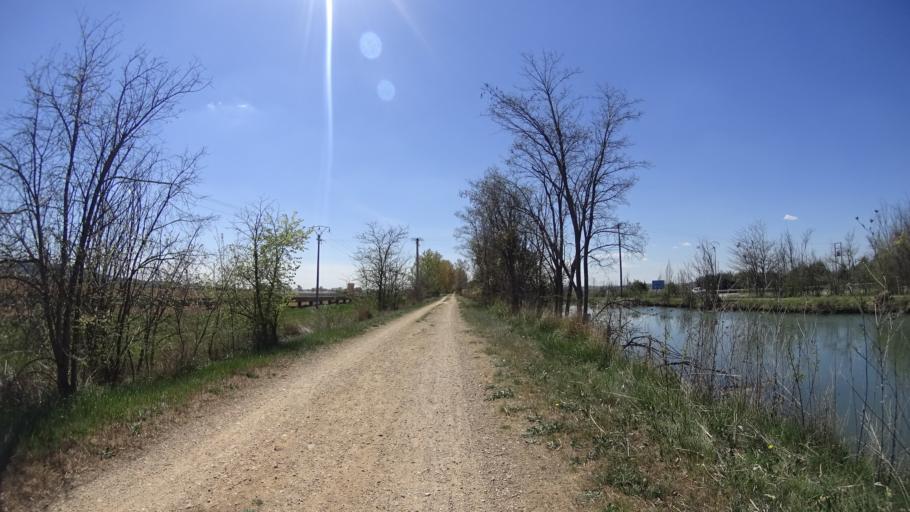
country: ES
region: Castille and Leon
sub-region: Provincia de Valladolid
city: Cabezon
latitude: 41.7498
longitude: -4.6467
